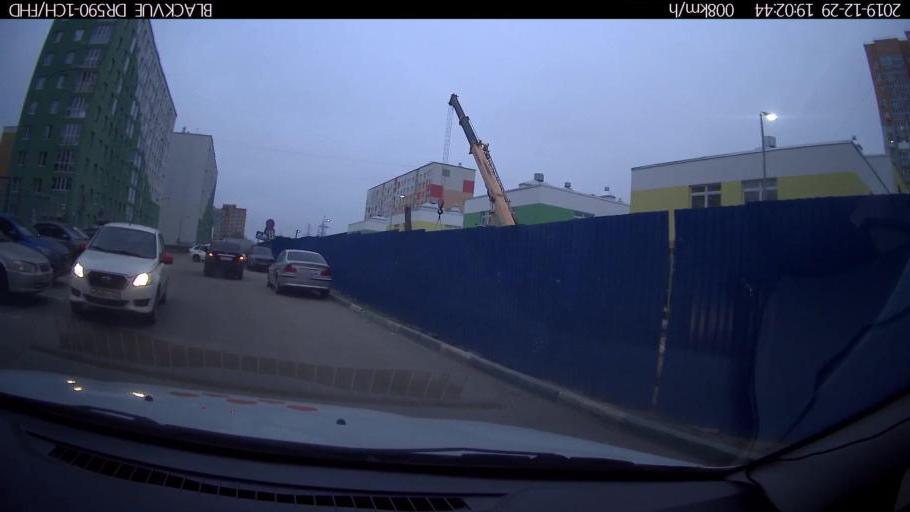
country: RU
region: Nizjnij Novgorod
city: Nizhniy Novgorod
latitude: 56.3427
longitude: 43.9147
